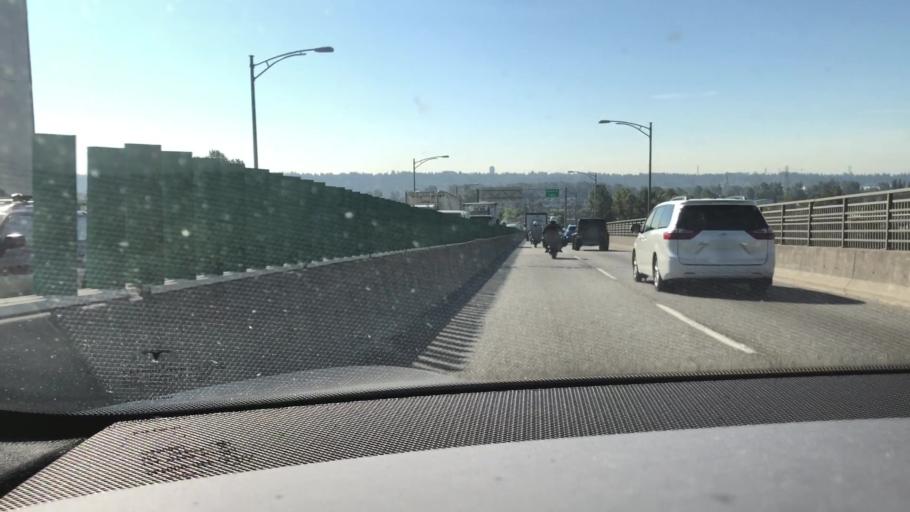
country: CA
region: British Columbia
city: New Westminster
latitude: 49.1949
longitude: -122.9440
